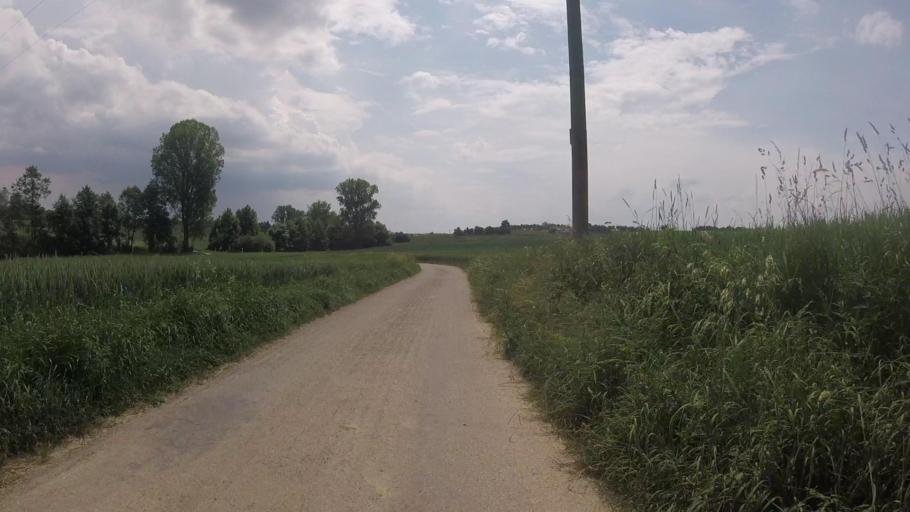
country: DE
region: Baden-Wuerttemberg
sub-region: Regierungsbezirk Stuttgart
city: Aspach
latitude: 48.9626
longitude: 9.4158
